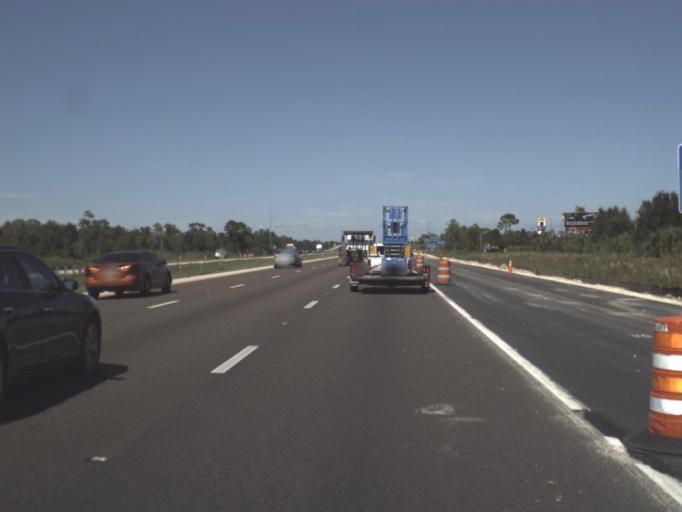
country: US
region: Florida
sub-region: Lee County
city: Gateway
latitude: 26.5379
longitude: -81.7947
